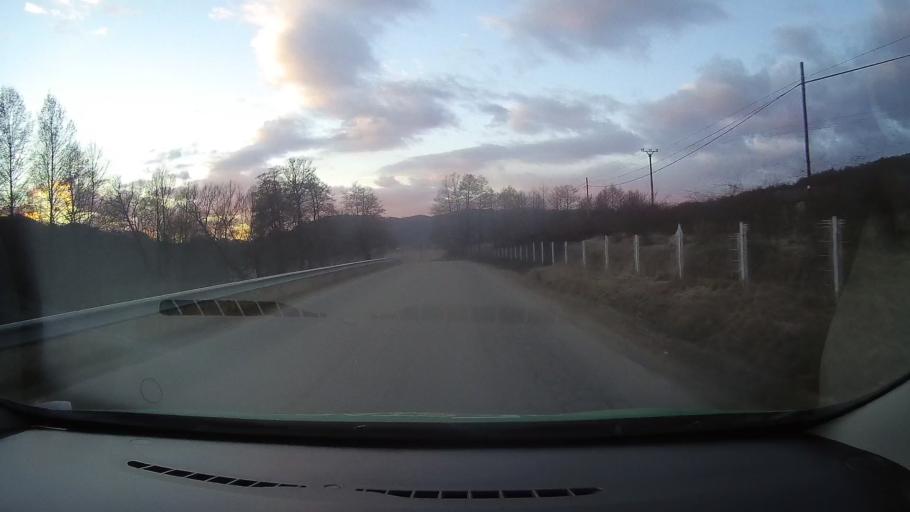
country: RO
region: Dambovita
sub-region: Comuna Valea Lunga
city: Valea Lunga Ogrea
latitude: 45.0604
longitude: 25.5941
